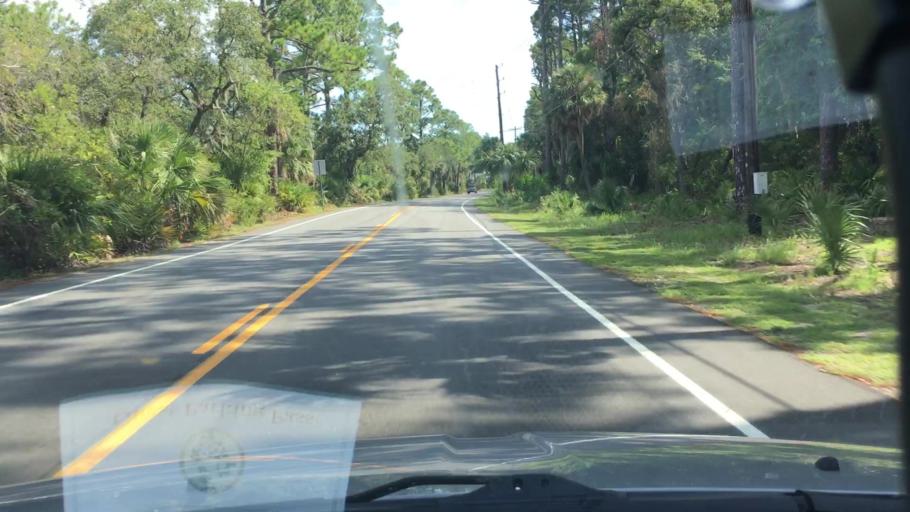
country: US
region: South Carolina
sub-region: Beaufort County
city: Beaufort
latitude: 32.3838
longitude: -80.4420
